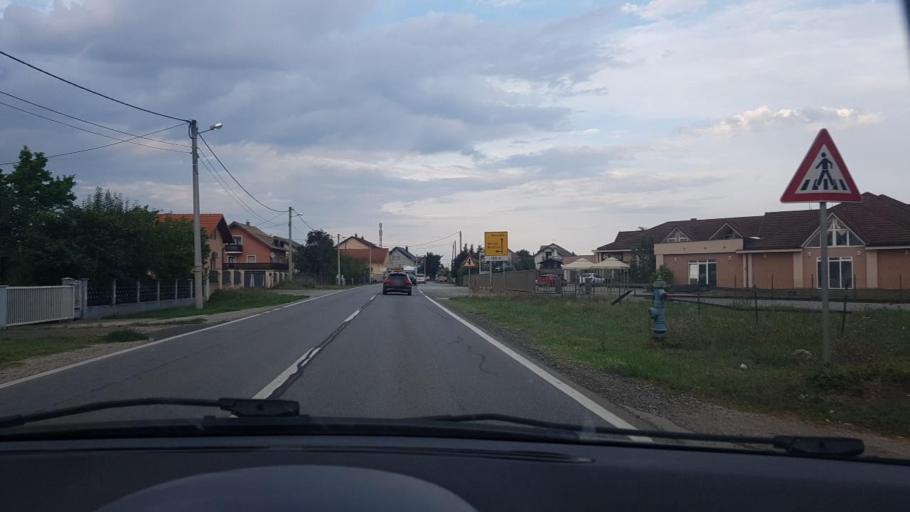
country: HR
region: Grad Zagreb
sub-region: Sesvete
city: Sesvete
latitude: 45.8806
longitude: 16.1713
